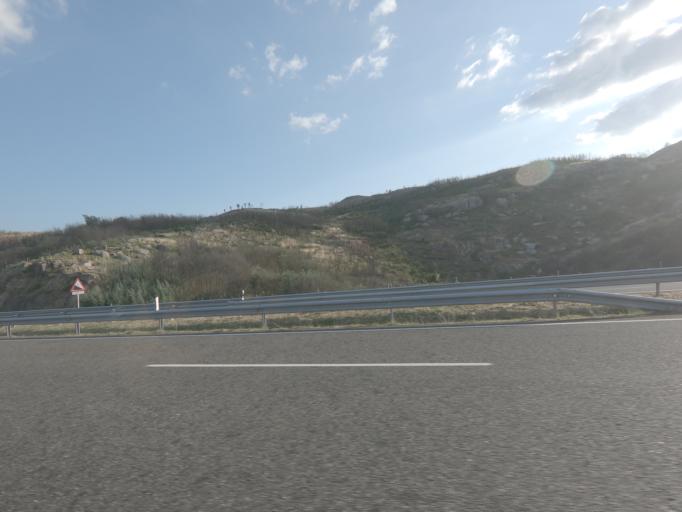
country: ES
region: Galicia
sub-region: Provincia de Ourense
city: Oimbra
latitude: 41.9401
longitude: -7.5003
